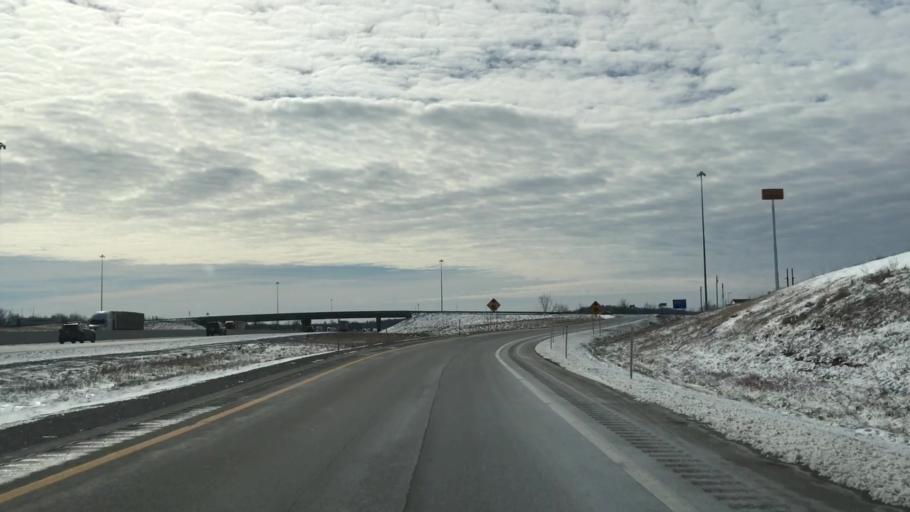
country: US
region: Kentucky
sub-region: Larue County
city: Hodgenville
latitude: 37.5246
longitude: -85.8846
